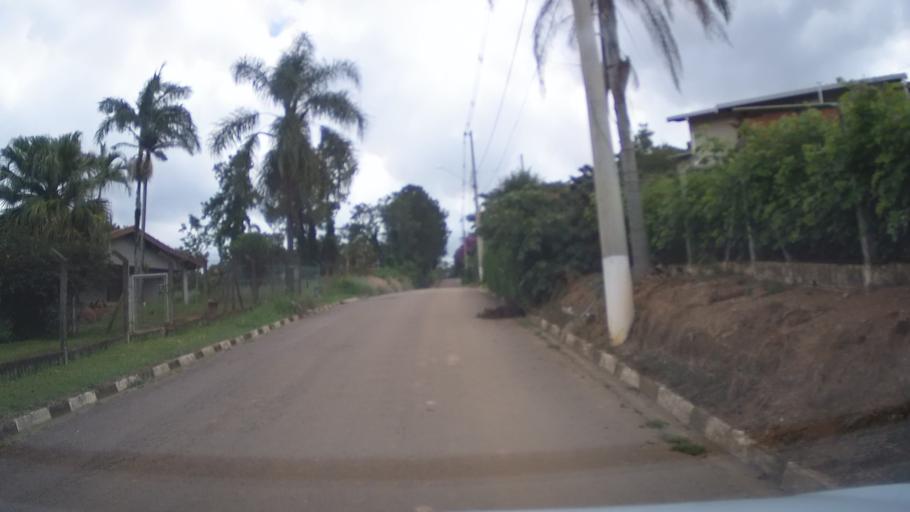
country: BR
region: Sao Paulo
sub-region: Vinhedo
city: Vinhedo
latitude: -23.0090
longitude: -46.9563
